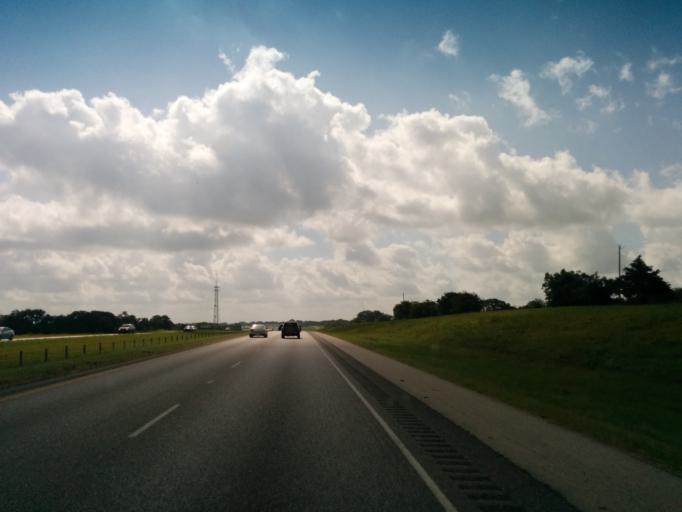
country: US
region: Texas
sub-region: Fayette County
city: Flatonia
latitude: 29.6934
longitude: -97.0190
